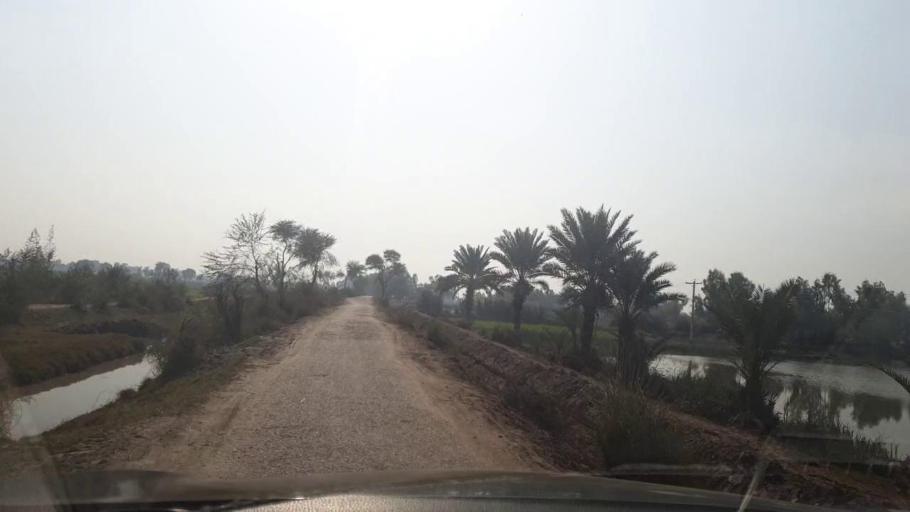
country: PK
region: Sindh
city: Khairpur
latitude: 28.1134
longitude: 69.6394
